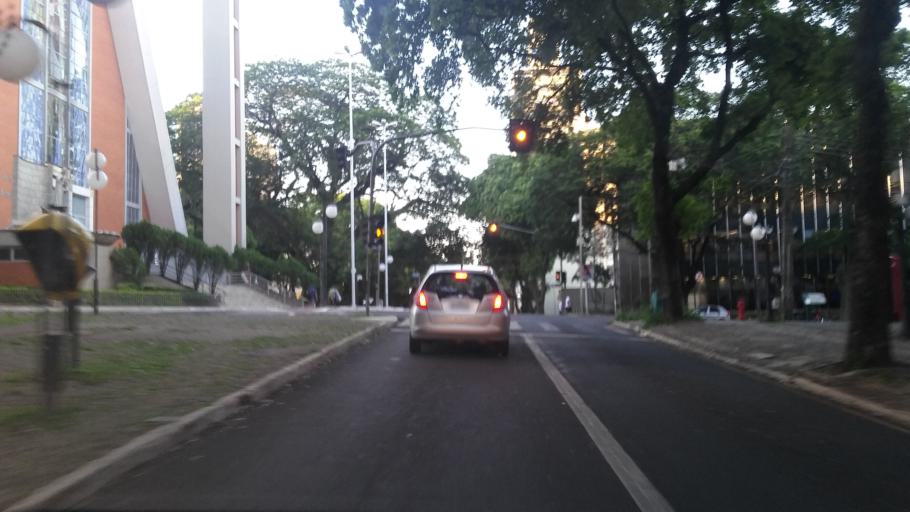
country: BR
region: Parana
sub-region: Londrina
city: Londrina
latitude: -23.3125
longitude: -51.1589
